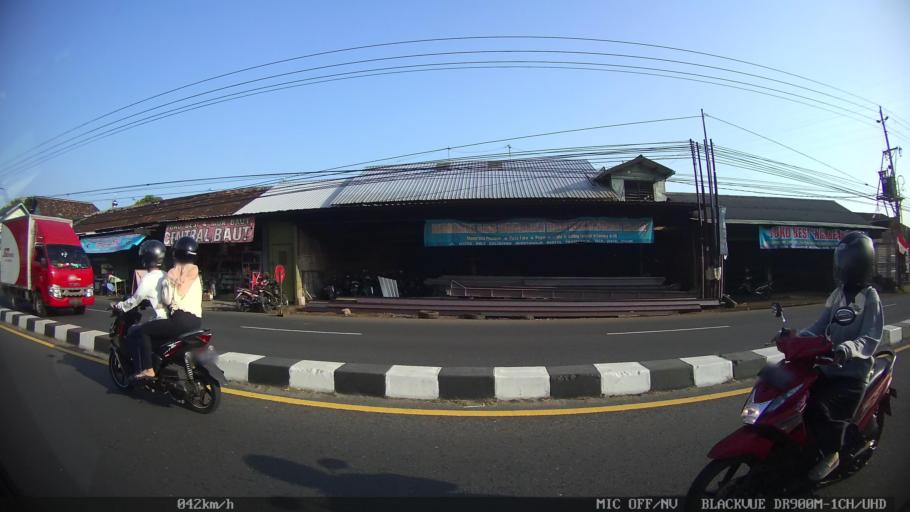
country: ID
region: Daerah Istimewa Yogyakarta
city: Gamping Lor
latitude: -7.8001
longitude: 110.3395
